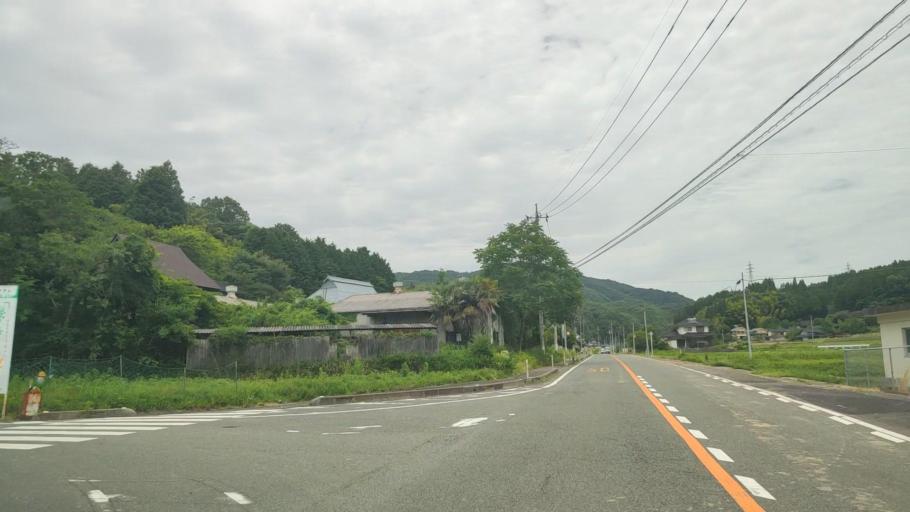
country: JP
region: Okayama
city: Tsuyama
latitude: 35.0799
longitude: 134.2477
